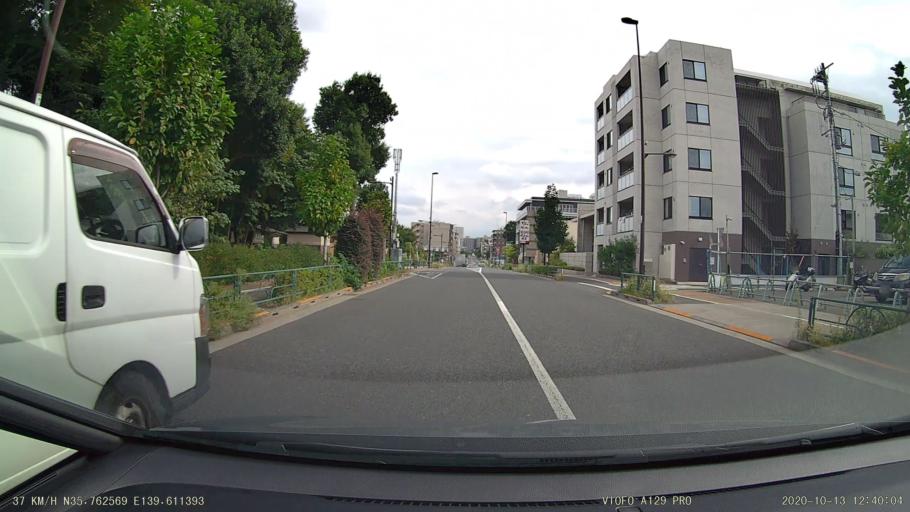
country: JP
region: Saitama
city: Wako
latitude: 35.7625
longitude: 139.6115
